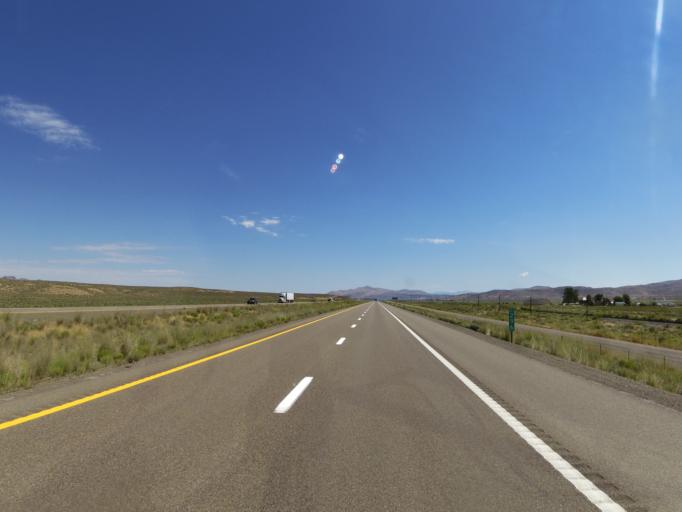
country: US
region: Nevada
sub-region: Elko County
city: Elko
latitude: 40.7872
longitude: -115.8635
